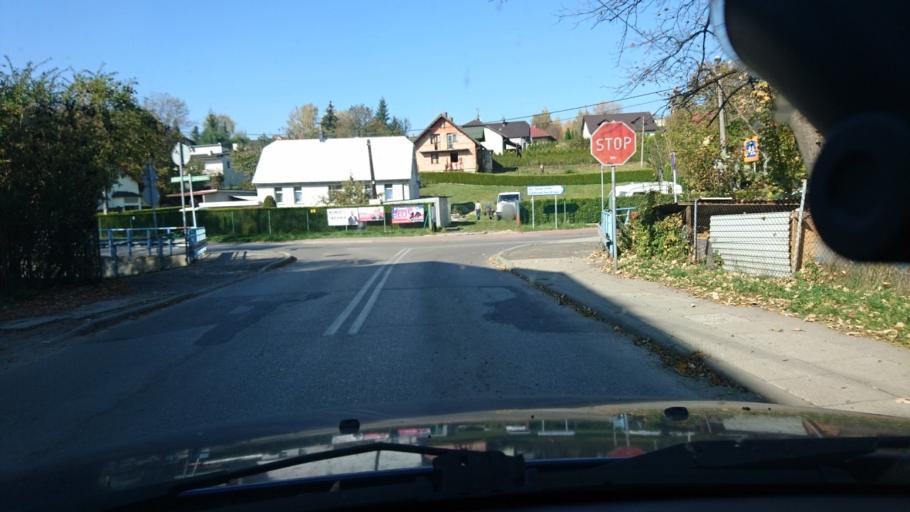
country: PL
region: Silesian Voivodeship
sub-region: Bielsko-Biala
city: Bielsko-Biala
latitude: 49.8302
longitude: 19.0316
